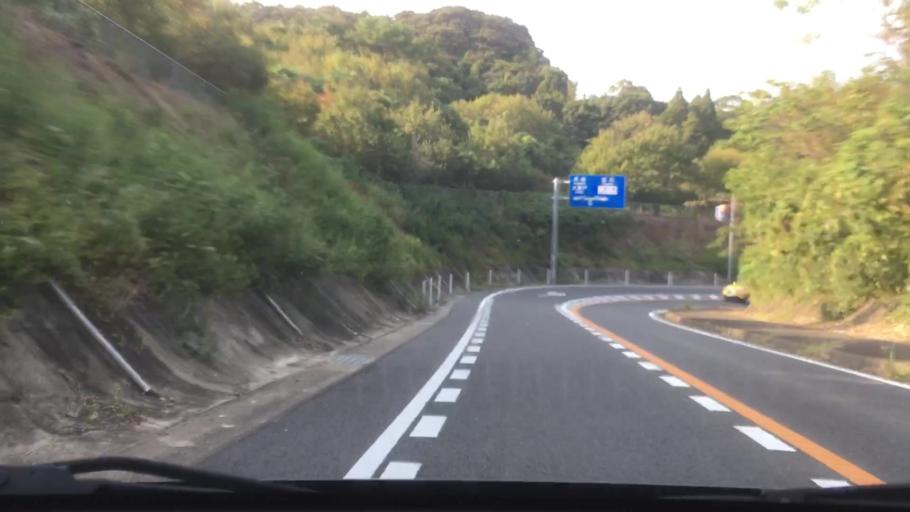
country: JP
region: Nagasaki
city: Sasebo
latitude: 33.0344
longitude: 129.6635
